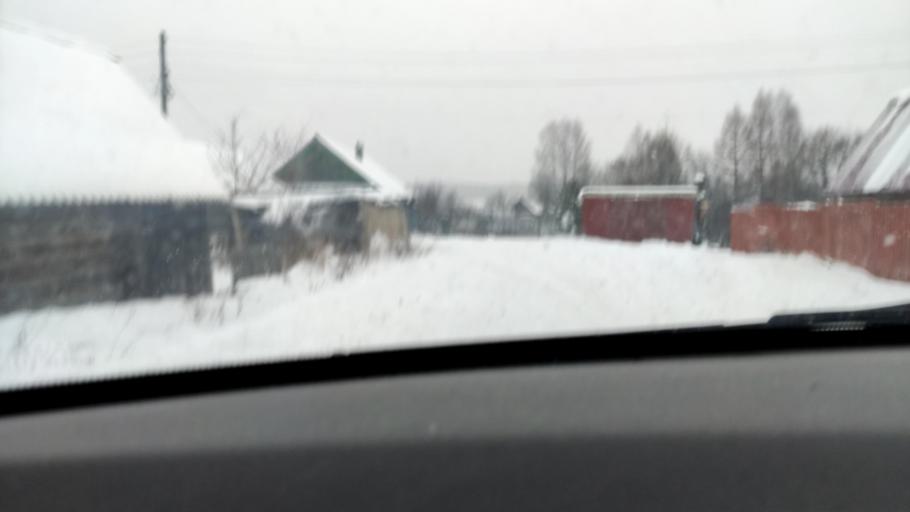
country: RU
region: Perm
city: Ust'-Kachka
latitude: 57.9396
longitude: 55.7461
